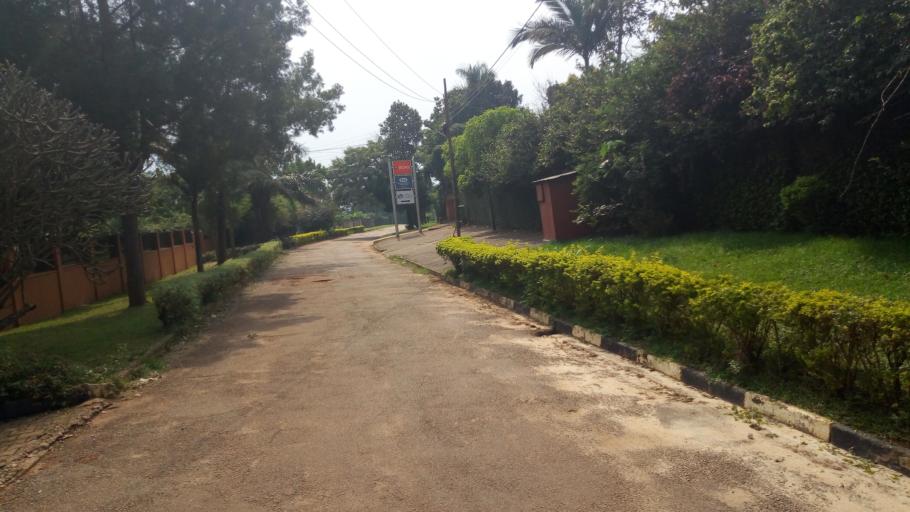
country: UG
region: Central Region
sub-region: Kampala District
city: Kampala
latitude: 0.3119
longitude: 32.6213
